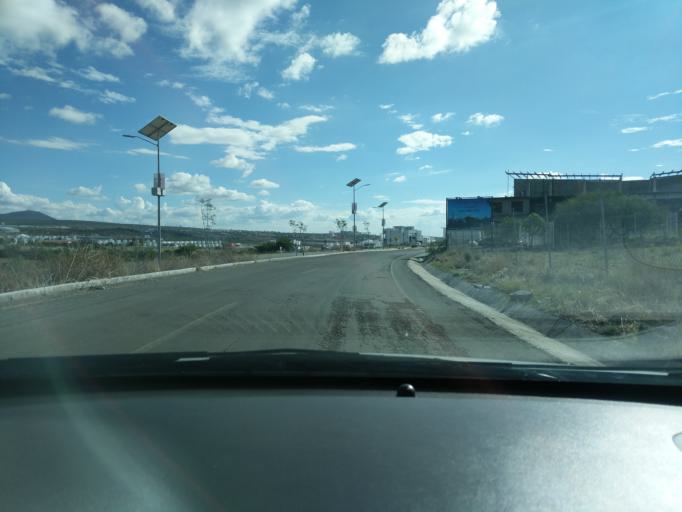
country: MX
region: Queretaro
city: La Canada
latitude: 20.5927
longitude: -100.3216
